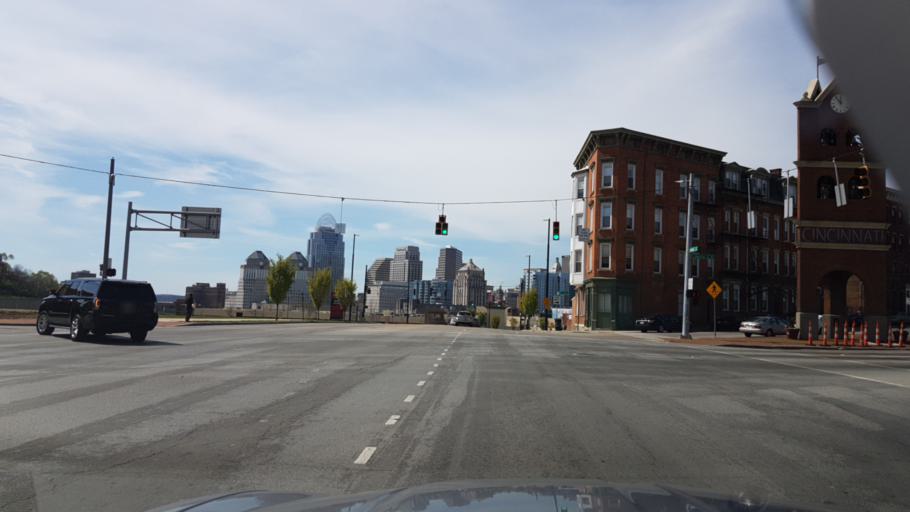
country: US
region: Kentucky
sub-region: Campbell County
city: Newport
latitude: 39.1114
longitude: -84.5038
